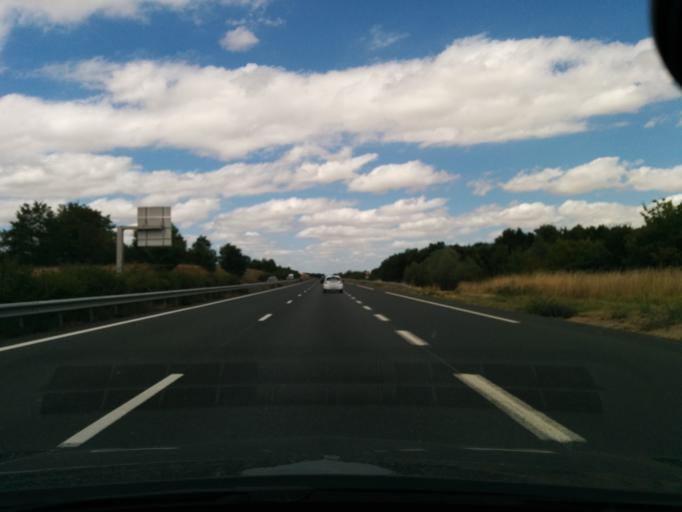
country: FR
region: Centre
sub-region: Departement de l'Indre
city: Saint-Maur
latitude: 46.7710
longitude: 1.6358
